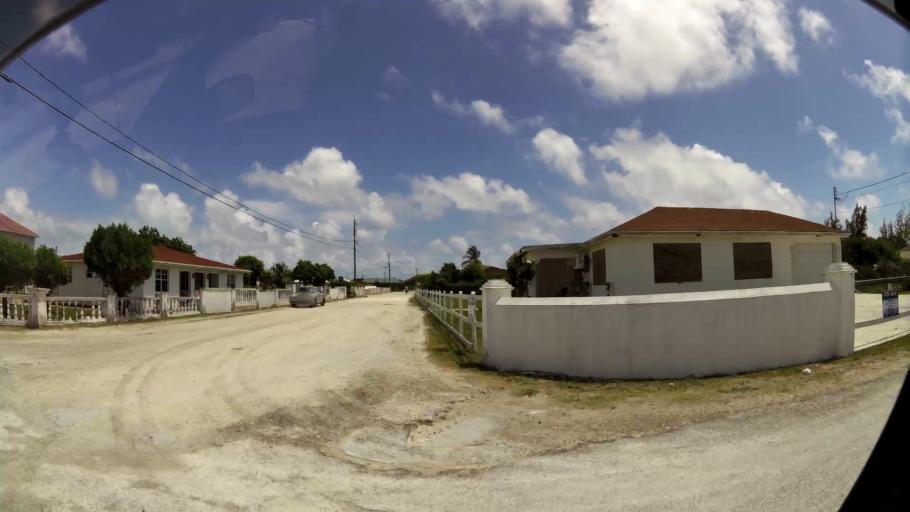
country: TC
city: Cockburn Town
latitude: 21.4545
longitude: -71.1467
